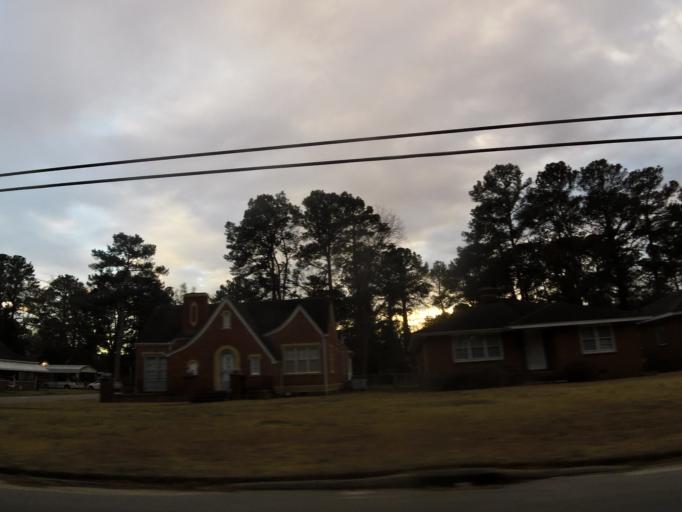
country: US
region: North Carolina
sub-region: Nash County
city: Rocky Mount
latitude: 35.9493
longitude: -77.8129
